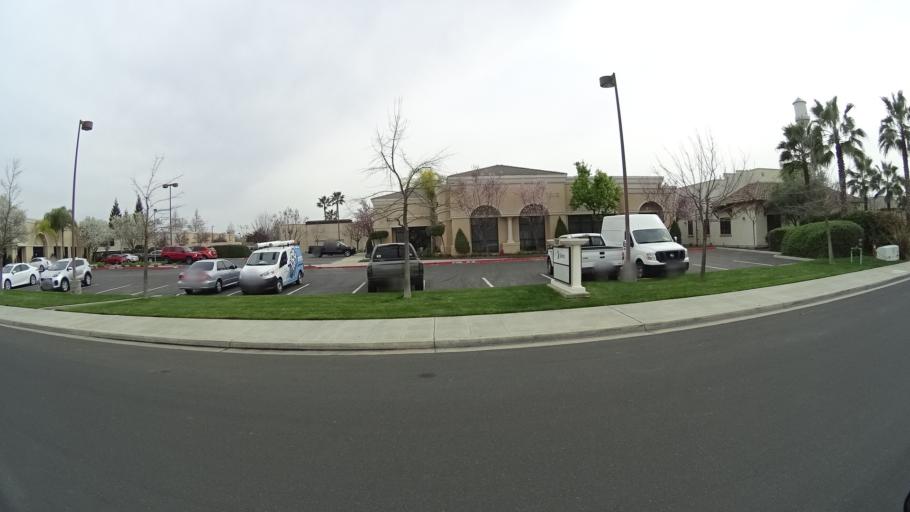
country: US
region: California
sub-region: Fresno County
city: Fresno
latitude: 36.8464
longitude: -119.8050
